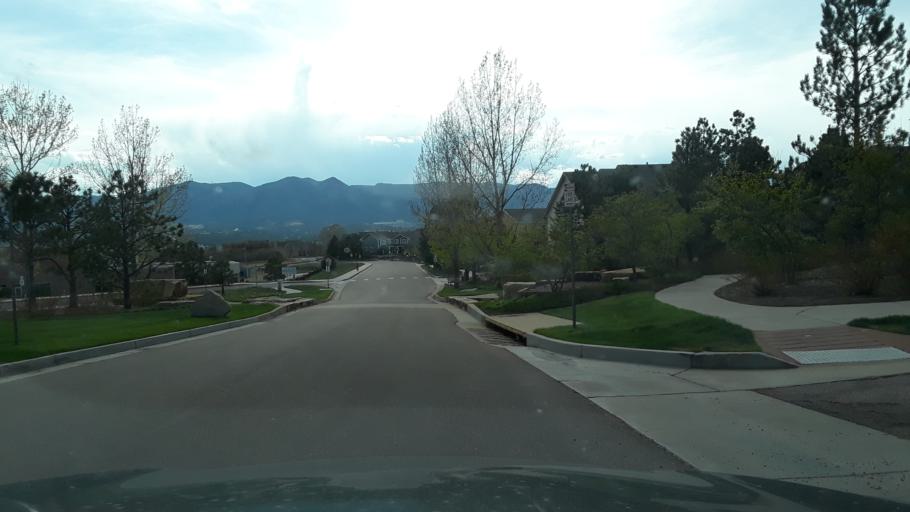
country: US
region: Colorado
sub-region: El Paso County
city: Gleneagle
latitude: 39.0132
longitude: -104.8023
